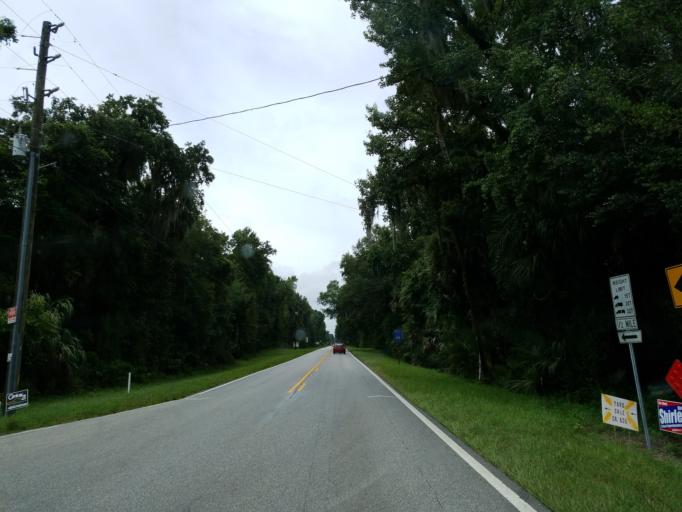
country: US
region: Florida
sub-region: Citrus County
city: Floral City
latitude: 28.7178
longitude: -82.2361
